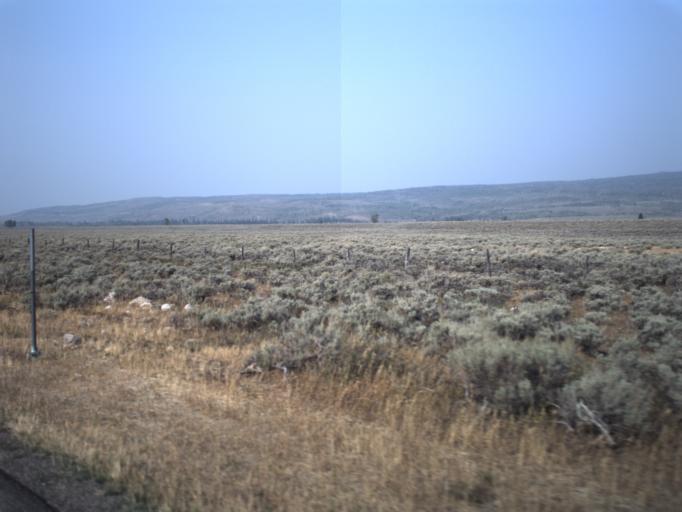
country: US
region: Wyoming
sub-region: Uinta County
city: Evanston
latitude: 40.9464
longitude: -110.8394
